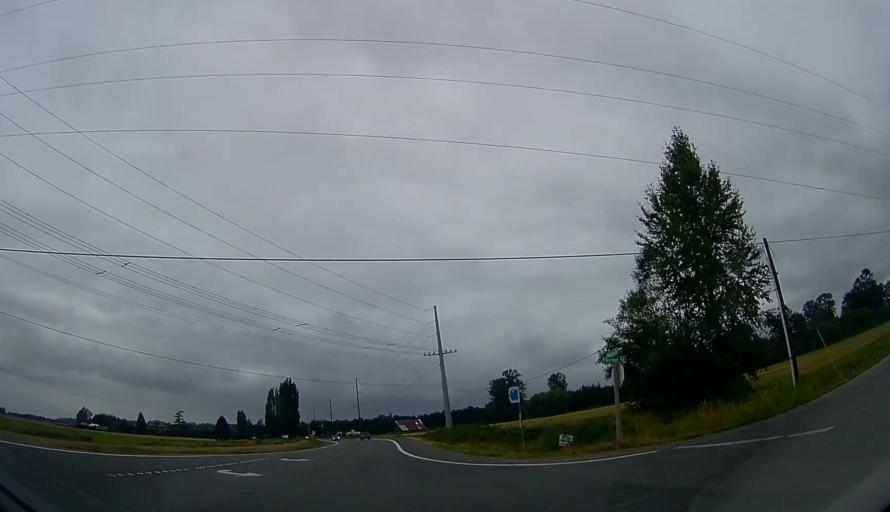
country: US
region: Washington
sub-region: Snohomish County
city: Stanwood
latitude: 48.2131
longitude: -122.3359
